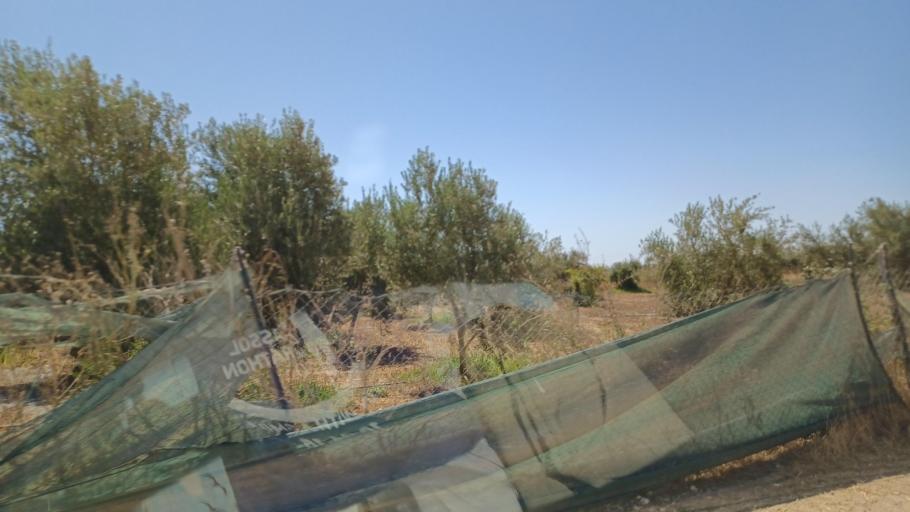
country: CY
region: Ammochostos
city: Avgorou
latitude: 35.0571
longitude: 33.8498
